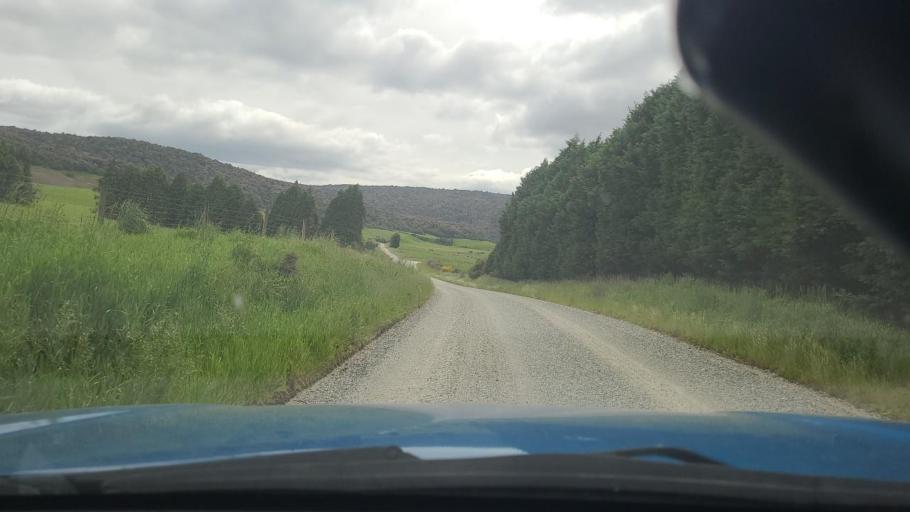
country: NZ
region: Otago
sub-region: Clutha District
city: Papatowai
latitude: -46.5130
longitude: 169.1457
